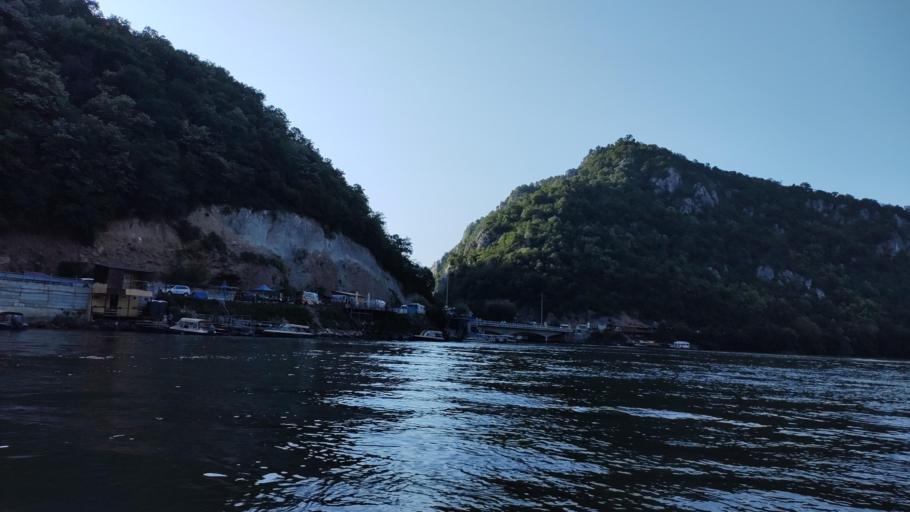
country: RO
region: Mehedinti
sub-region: Comuna Dubova
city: Dubova
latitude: 44.6379
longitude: 22.2949
